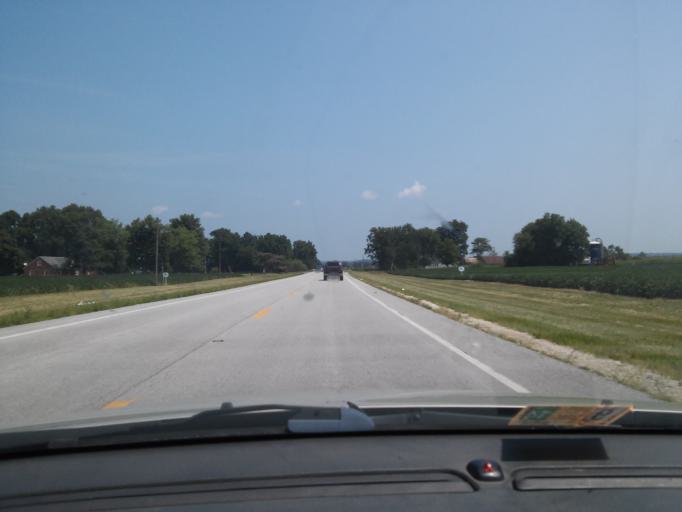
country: US
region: Missouri
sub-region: Pike County
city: Louisiana
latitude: 39.4858
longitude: -91.0131
